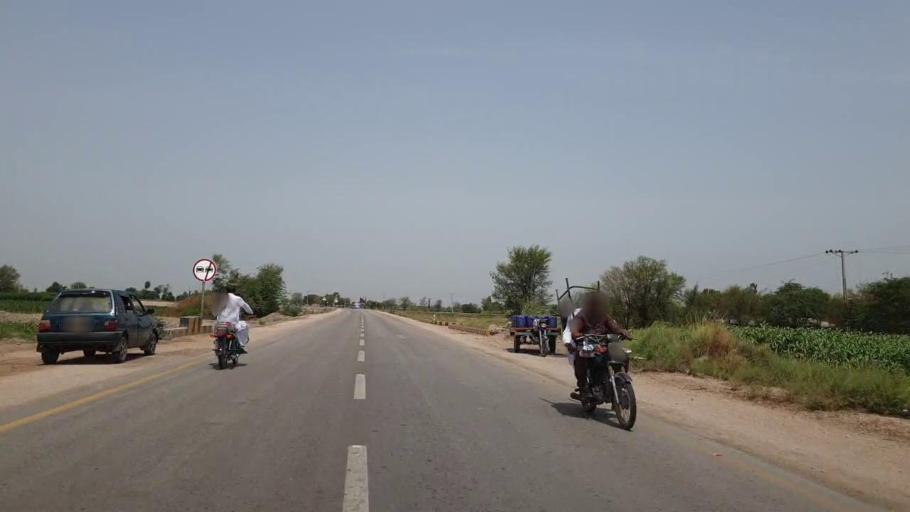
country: PK
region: Sindh
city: Shahpur Chakar
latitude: 26.1916
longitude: 68.5769
